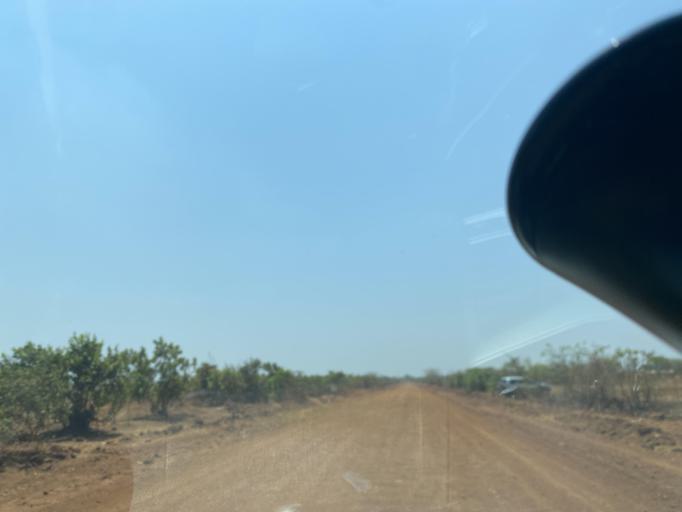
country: ZM
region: Lusaka
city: Lusaka
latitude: -15.4556
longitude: 27.9414
